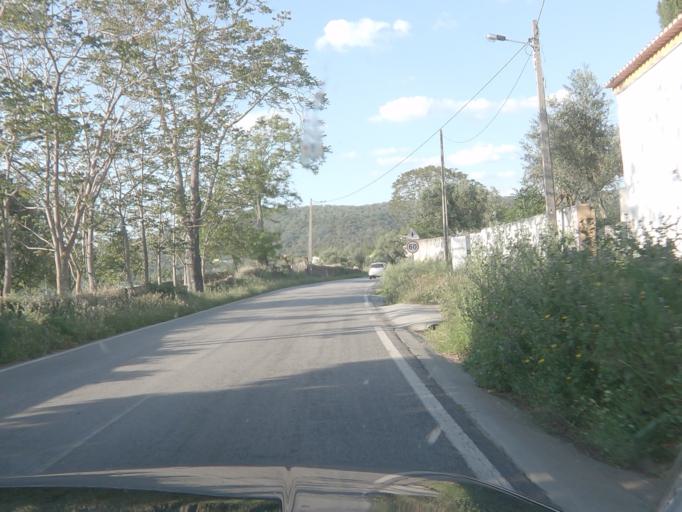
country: PT
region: Portalegre
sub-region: Portalegre
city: Portalegre
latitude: 39.3199
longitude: -7.4388
